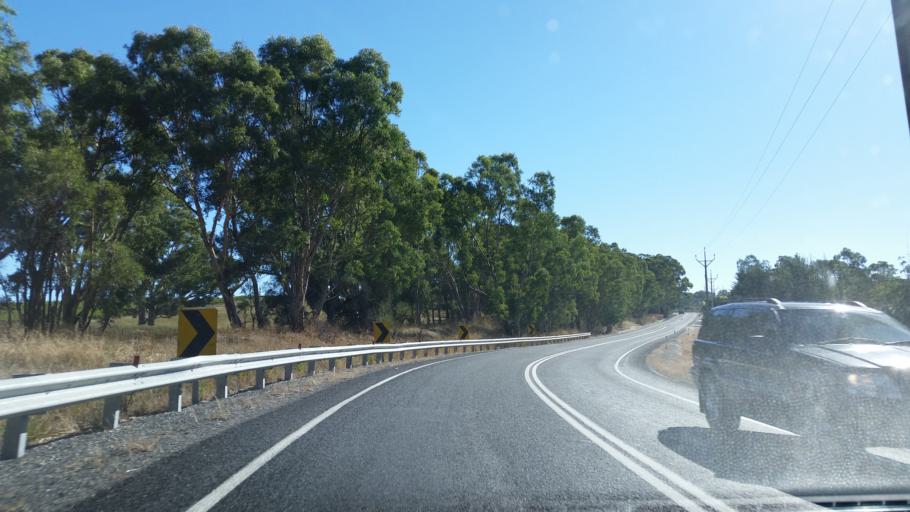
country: AU
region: South Australia
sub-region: Adelaide Hills
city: Birdwood
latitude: -34.8063
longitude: 138.9867
